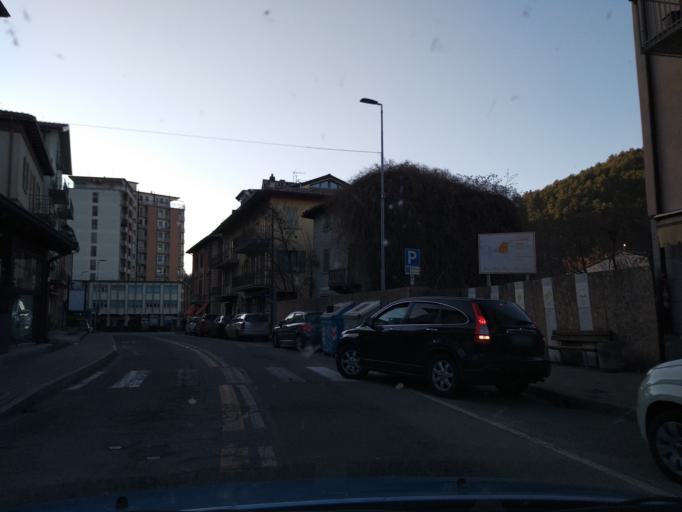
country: IT
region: Emilia-Romagna
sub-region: Provincia di Reggio Emilia
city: Castelnovo ne'Monti
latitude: 44.4363
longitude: 10.4041
